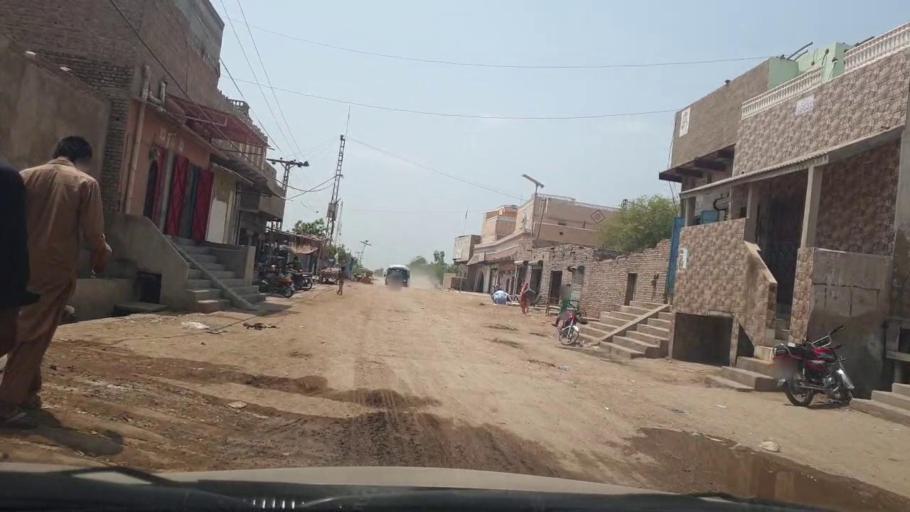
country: PK
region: Sindh
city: Ratodero
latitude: 27.7235
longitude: 68.2810
